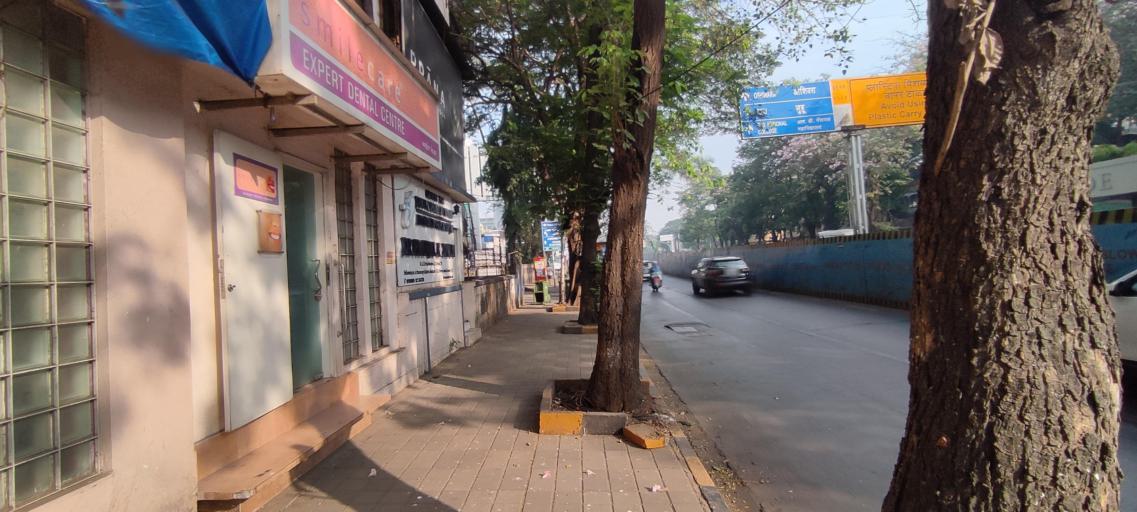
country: IN
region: Maharashtra
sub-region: Mumbai Suburban
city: Mumbai
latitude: 19.0584
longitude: 72.8366
